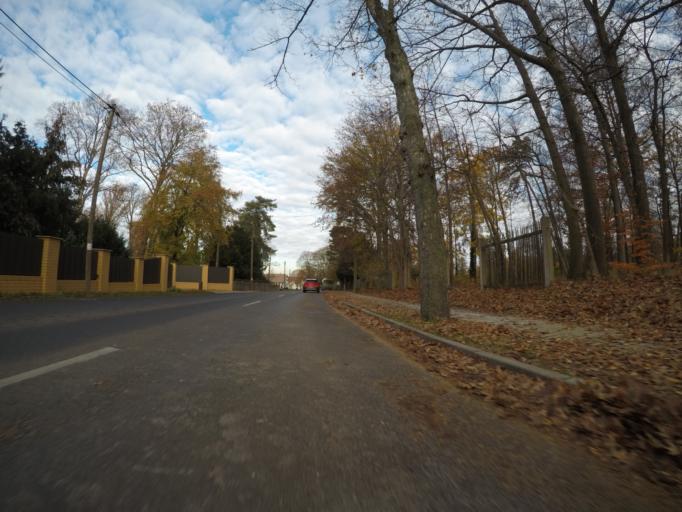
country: DE
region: Saxony
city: Meerane
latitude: 50.8514
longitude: 12.4456
